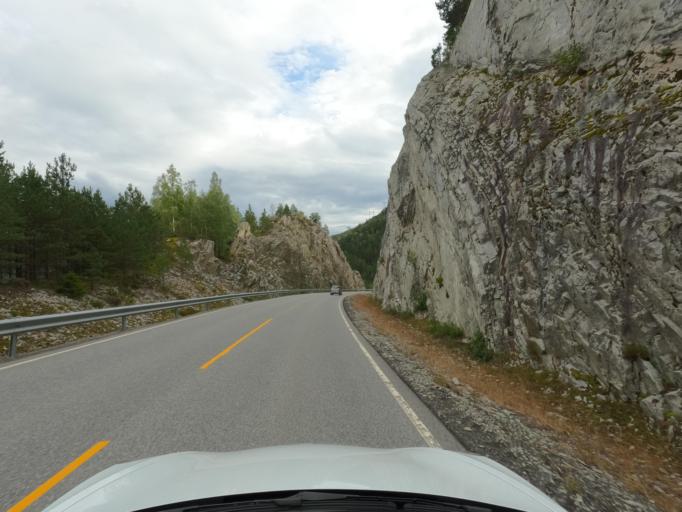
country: NO
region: Telemark
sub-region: Hjartdal
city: Sauland
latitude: 59.7942
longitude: 9.0010
